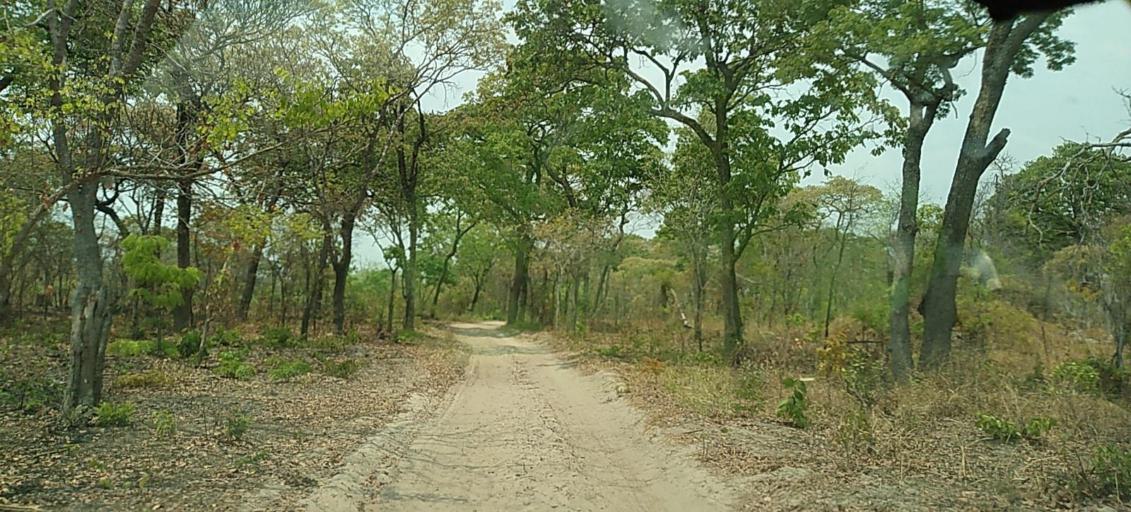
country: ZM
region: North-Western
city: Kabompo
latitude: -13.5462
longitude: 24.4504
